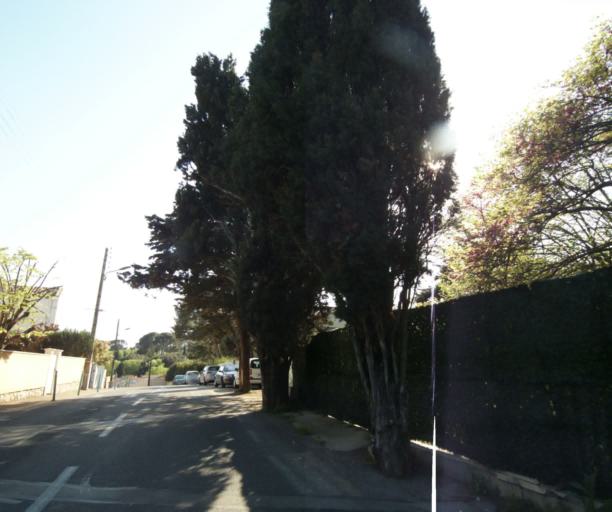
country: FR
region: Languedoc-Roussillon
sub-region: Departement de l'Herault
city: Castelnau-le-Lez
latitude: 43.6393
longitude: 3.9045
